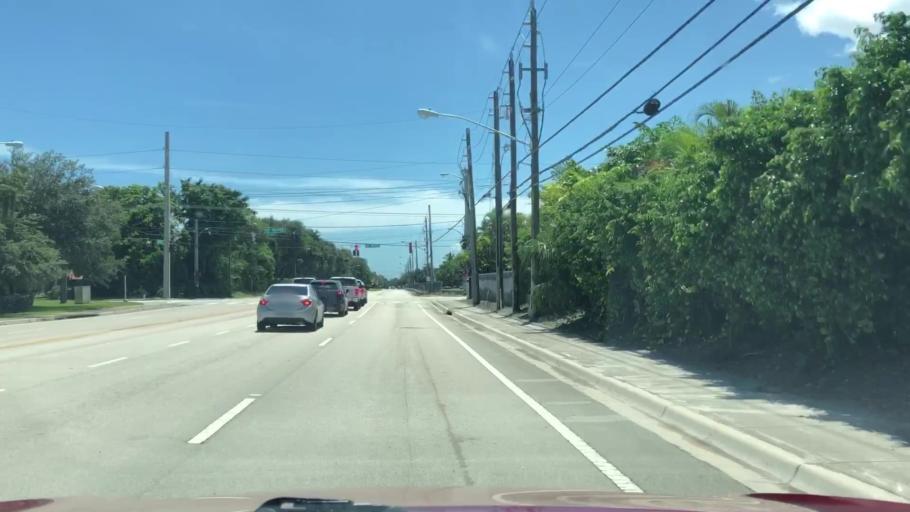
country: US
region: Florida
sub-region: Palm Beach County
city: Boynton Beach
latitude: 26.5326
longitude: -80.1067
